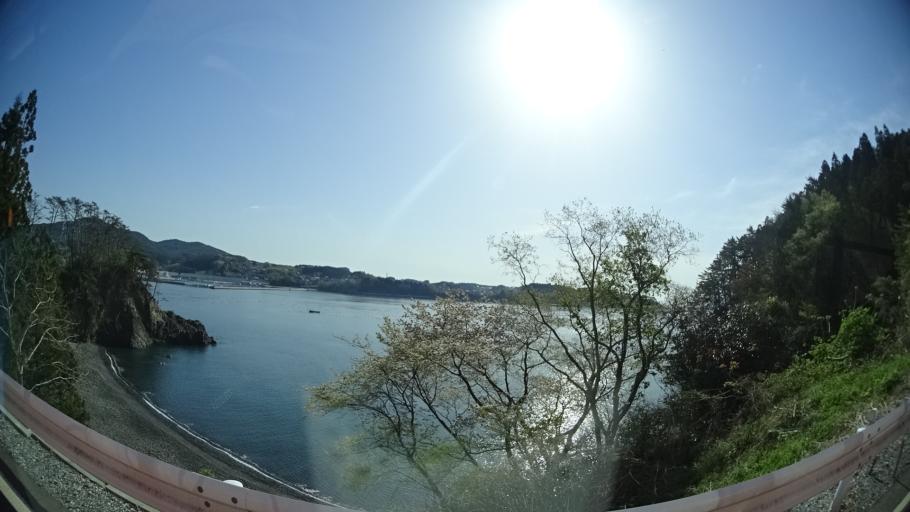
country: JP
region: Iwate
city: Ofunato
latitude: 38.9915
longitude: 141.7120
